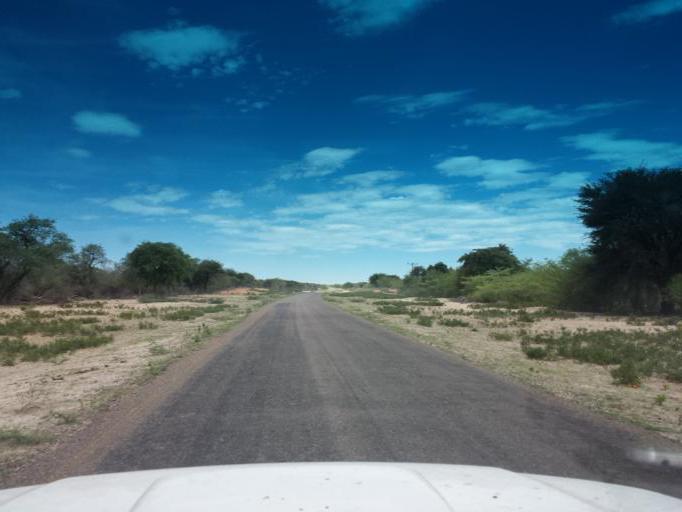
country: BW
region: North West
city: Shakawe
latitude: -18.7135
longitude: 22.1393
